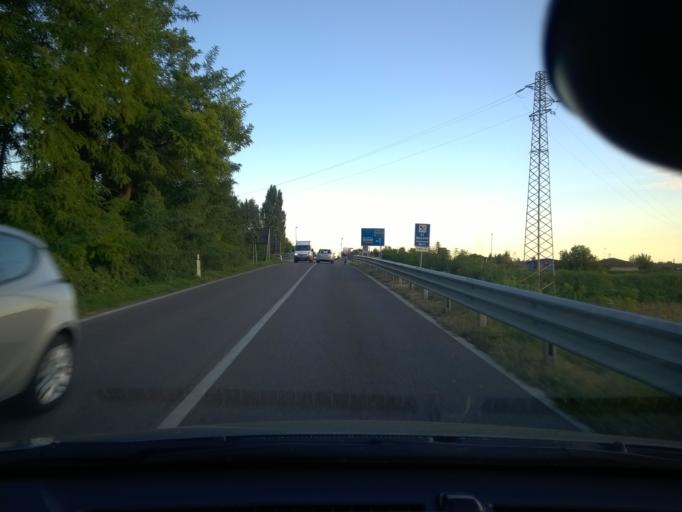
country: IT
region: Veneto
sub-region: Provincia di Treviso
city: Motta di Livenza
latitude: 45.7653
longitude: 12.6150
